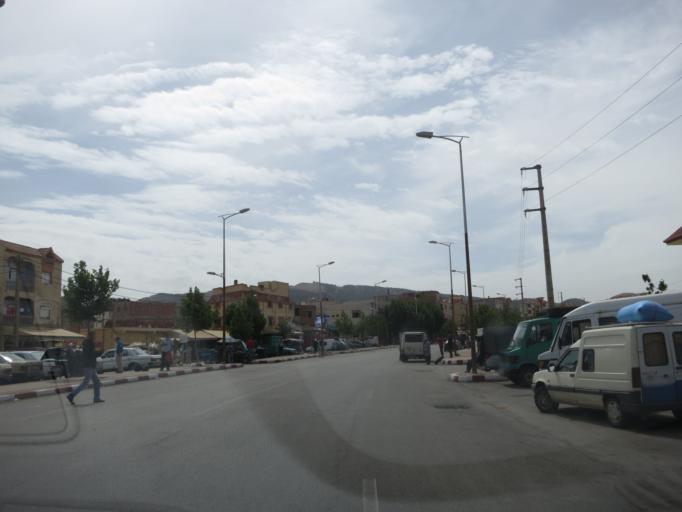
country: MA
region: Meknes-Tafilalet
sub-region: Ifrane
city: Azrou
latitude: 33.2366
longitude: -5.0592
